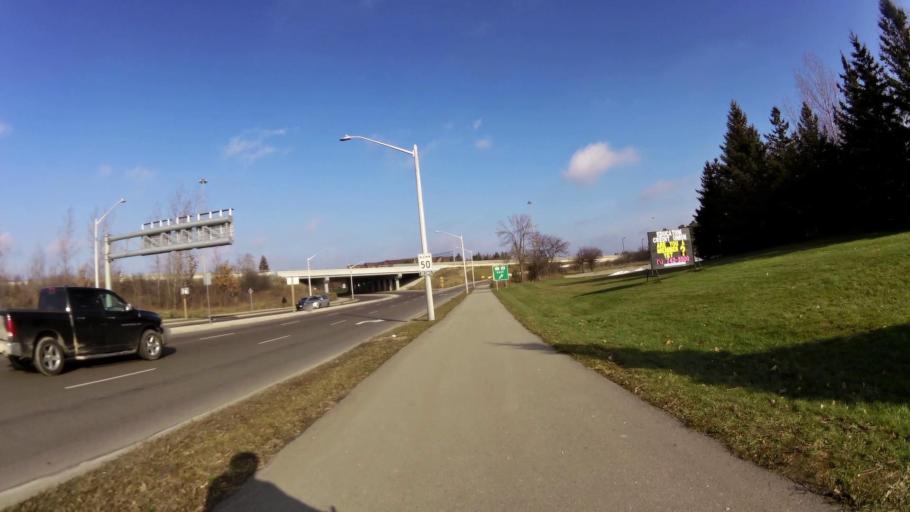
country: CA
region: Ontario
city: Kitchener
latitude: 43.4268
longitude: -80.4816
